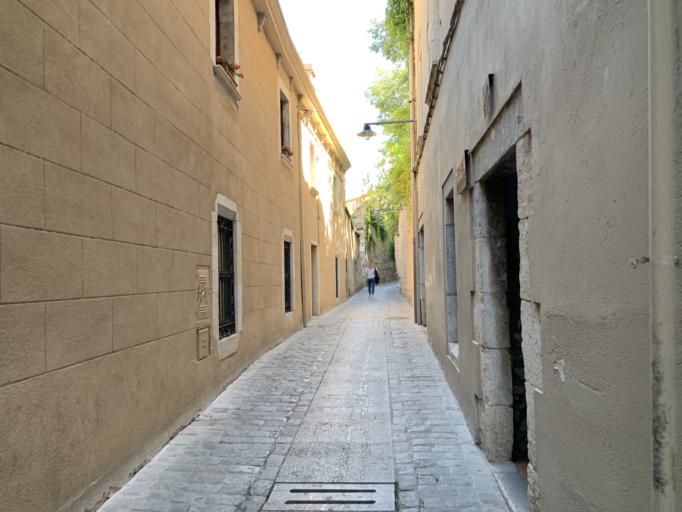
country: ES
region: Catalonia
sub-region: Provincia de Girona
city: Girona
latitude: 41.9841
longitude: 2.8272
